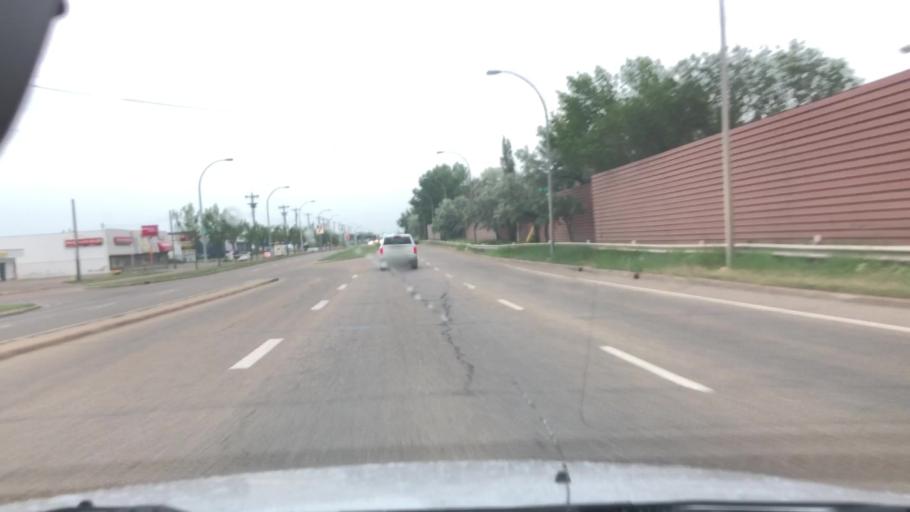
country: CA
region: Alberta
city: St. Albert
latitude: 53.5589
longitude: -113.5995
